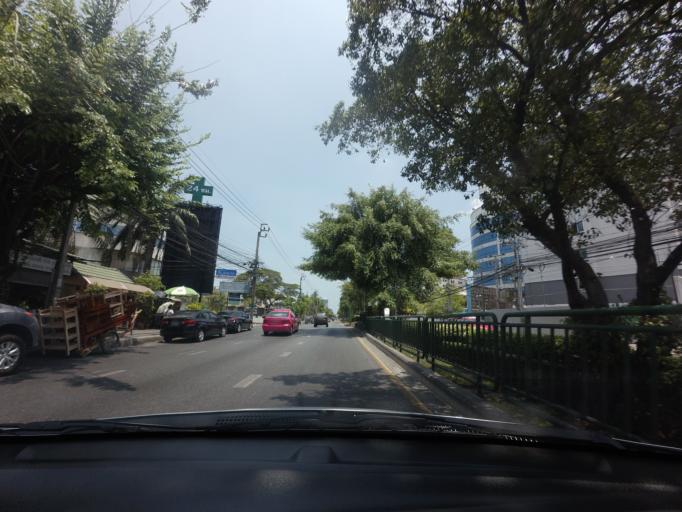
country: TH
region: Bangkok
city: Khan Na Yao
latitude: 13.8335
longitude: 100.6603
